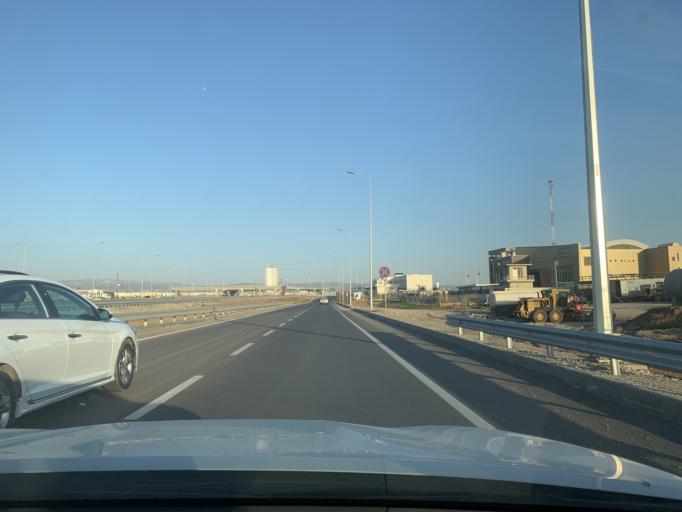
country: IQ
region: Arbil
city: Erbil
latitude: 36.2885
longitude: 44.0278
